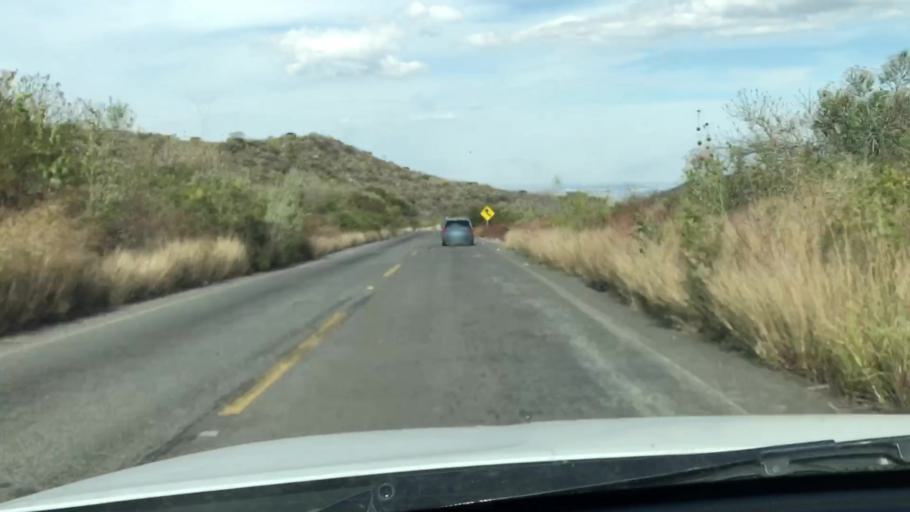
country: MX
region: Jalisco
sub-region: Zacoalco de Torres
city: Barranca de Otates (Barranca de Otatan)
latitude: 20.2383
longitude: -103.6850
